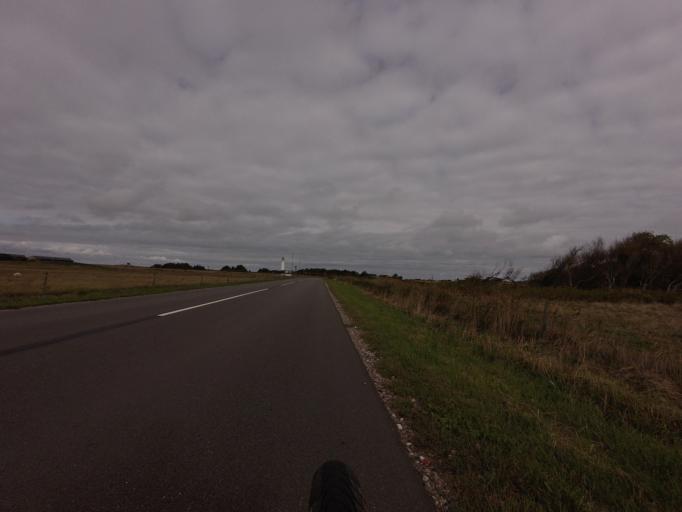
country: DK
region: North Denmark
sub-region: Hjorring Kommune
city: Hirtshals
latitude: 57.5798
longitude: 9.9443
